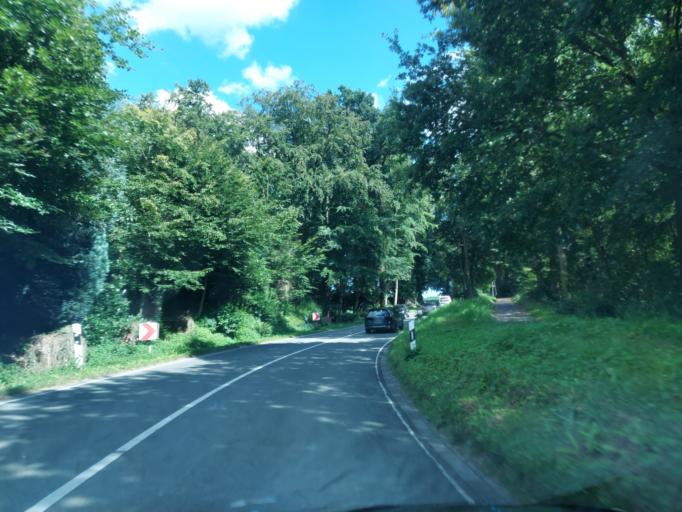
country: DE
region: Lower Saxony
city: Hagen
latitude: 52.1842
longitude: 7.9915
